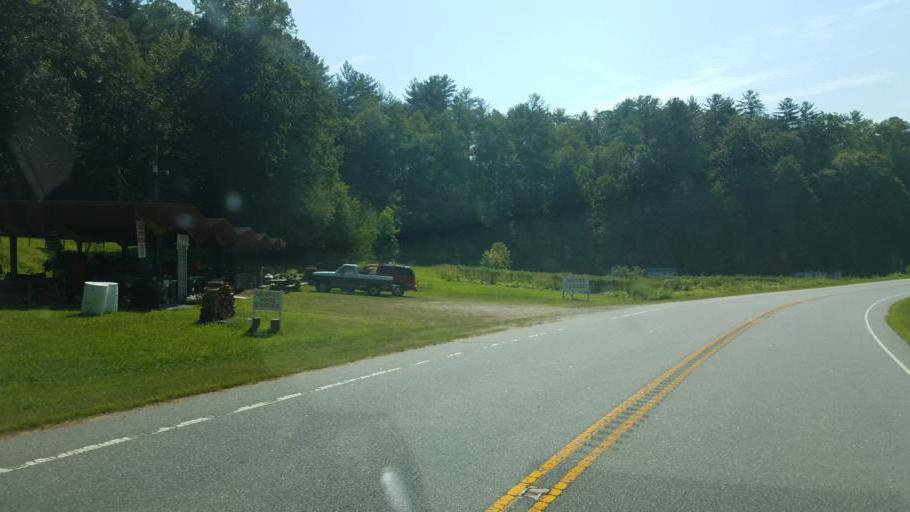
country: US
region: North Carolina
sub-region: Burke County
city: Glen Alpine
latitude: 35.8645
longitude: -81.7916
